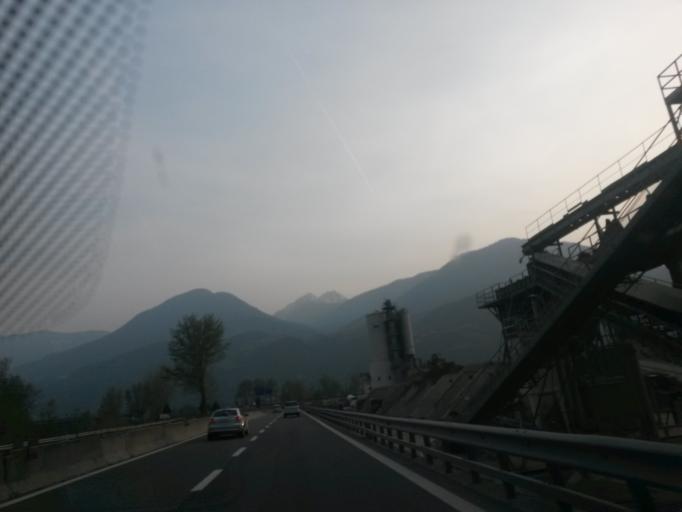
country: IT
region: Trentino-Alto Adige
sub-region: Bolzano
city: Postal
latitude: 46.6140
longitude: 11.1818
